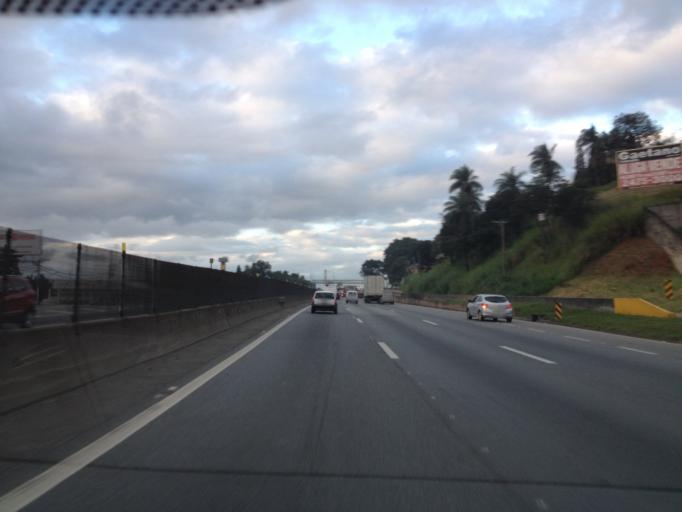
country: BR
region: Sao Paulo
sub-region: Itaquaquecetuba
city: Itaquaquecetuba
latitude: -23.4257
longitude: -46.4036
